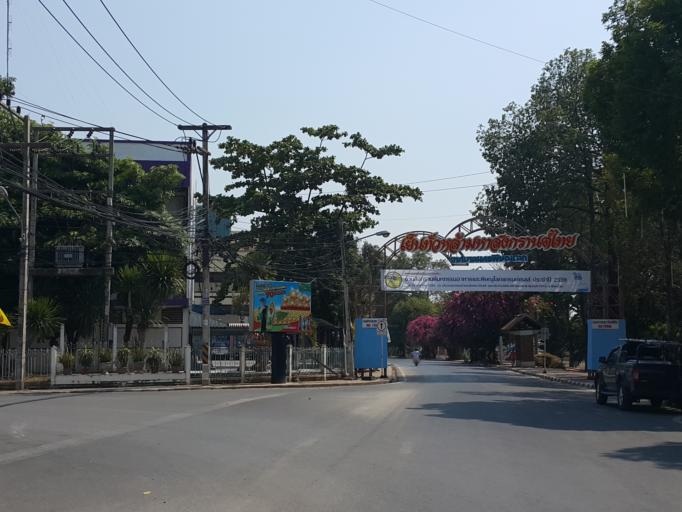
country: TH
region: Phitsanulok
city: Phitsanulok
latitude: 16.8219
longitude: 100.2603
